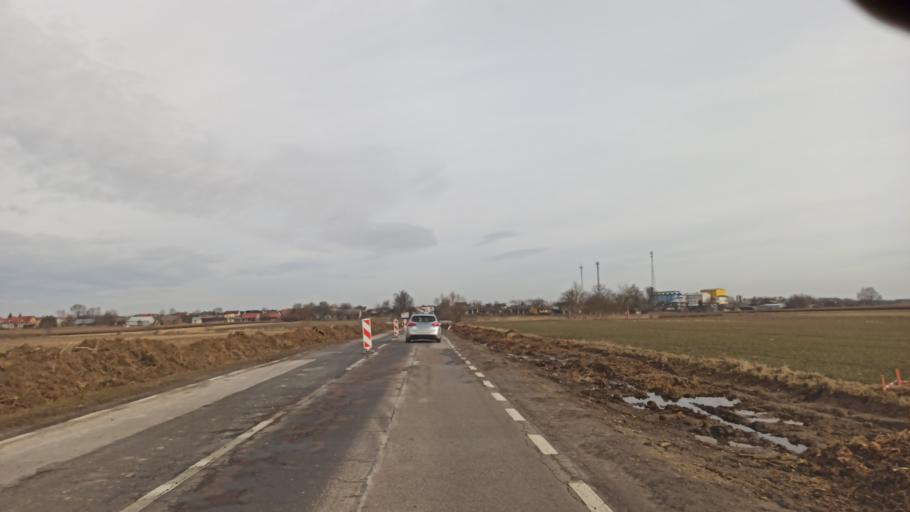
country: PL
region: Lublin Voivodeship
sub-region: Powiat bilgorajski
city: Tarnogrod
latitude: 50.3445
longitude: 22.7335
